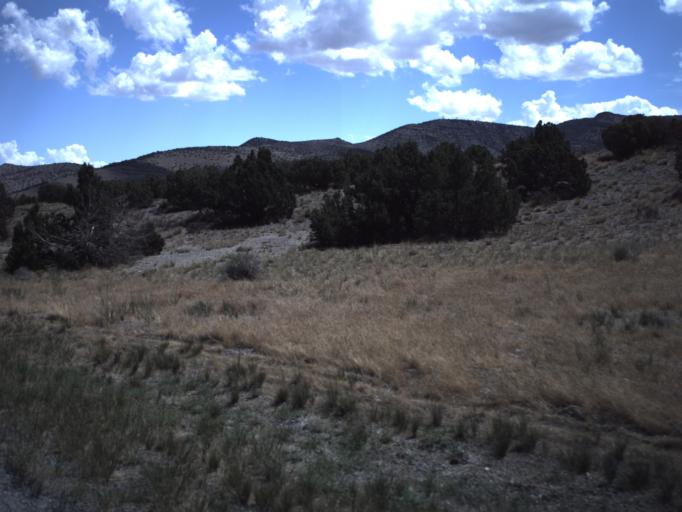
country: US
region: Utah
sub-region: Beaver County
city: Milford
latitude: 39.0761
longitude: -113.6293
